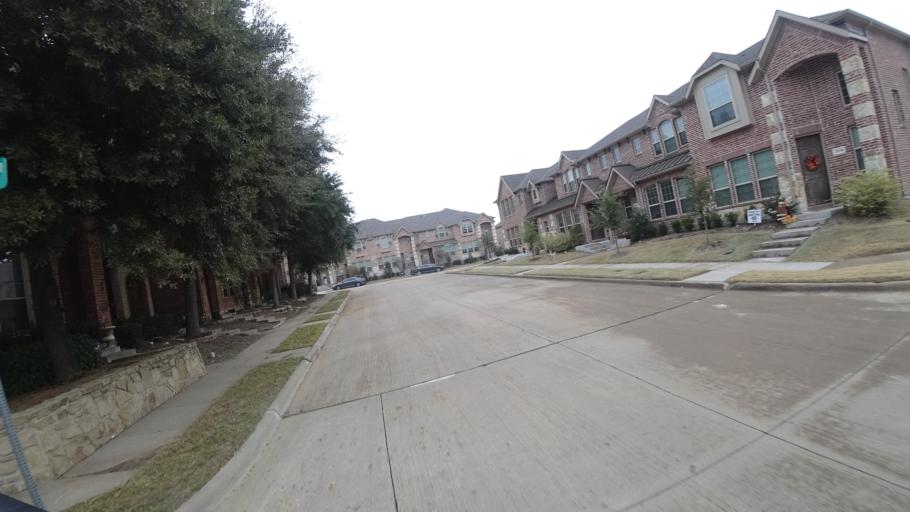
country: US
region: Texas
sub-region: Denton County
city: The Colony
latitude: 33.0639
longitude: -96.9143
